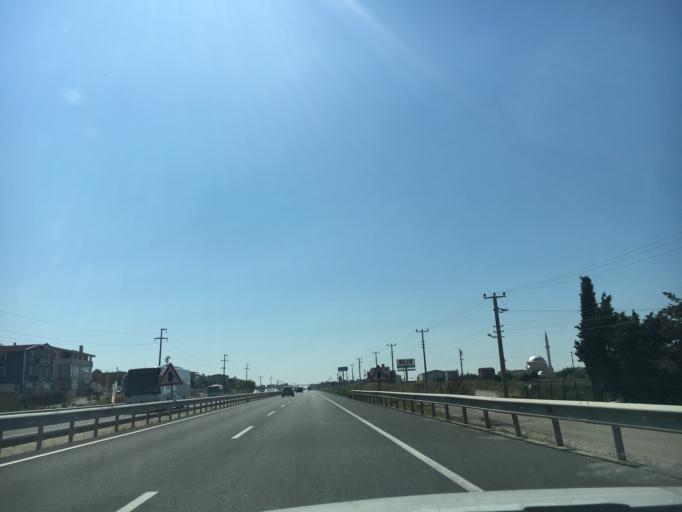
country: TR
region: Tekirdag
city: Marmara Ereglisi
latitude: 40.9836
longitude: 27.8607
